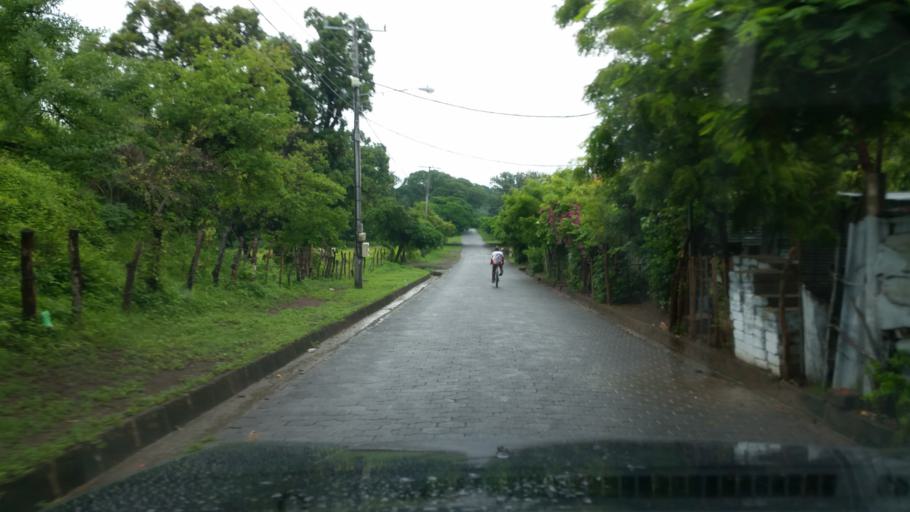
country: NI
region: Granada
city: Granada
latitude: 11.9228
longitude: -85.9477
